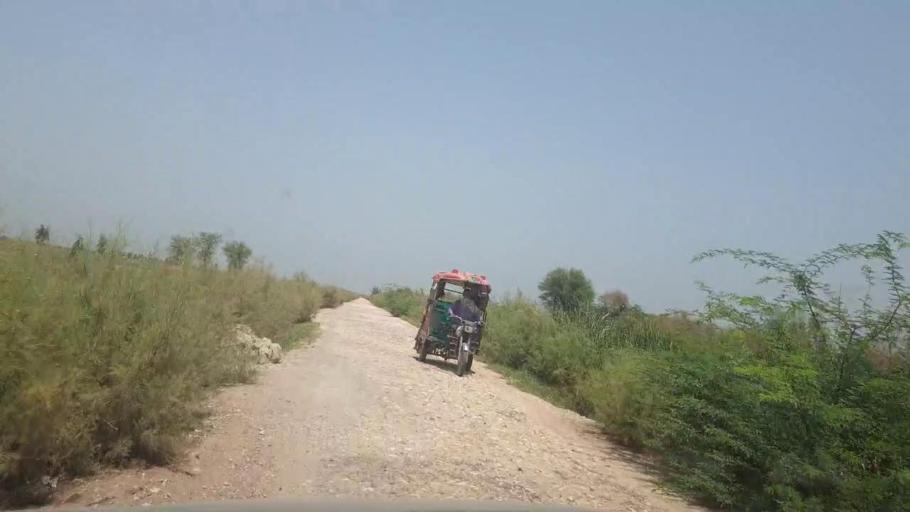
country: PK
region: Sindh
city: Lakhi
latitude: 27.8392
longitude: 68.6260
